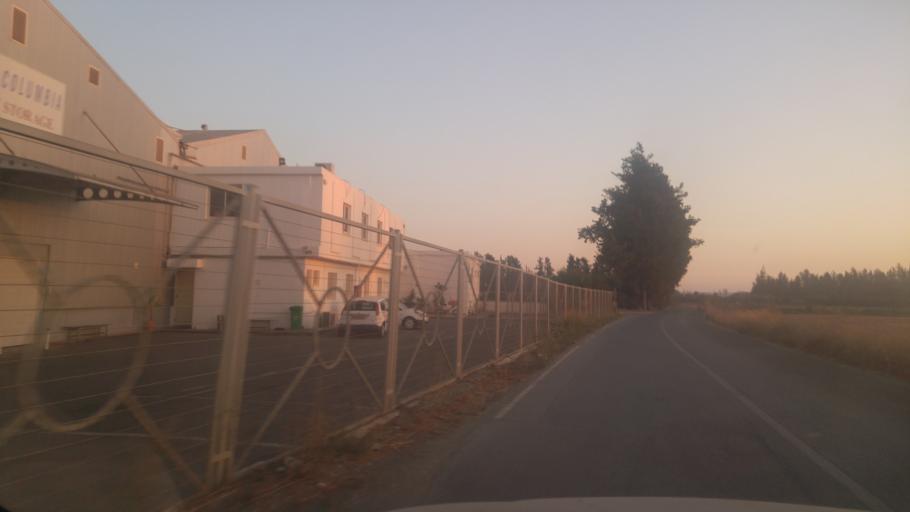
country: CY
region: Limassol
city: Ypsonas
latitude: 34.6588
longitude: 32.9902
